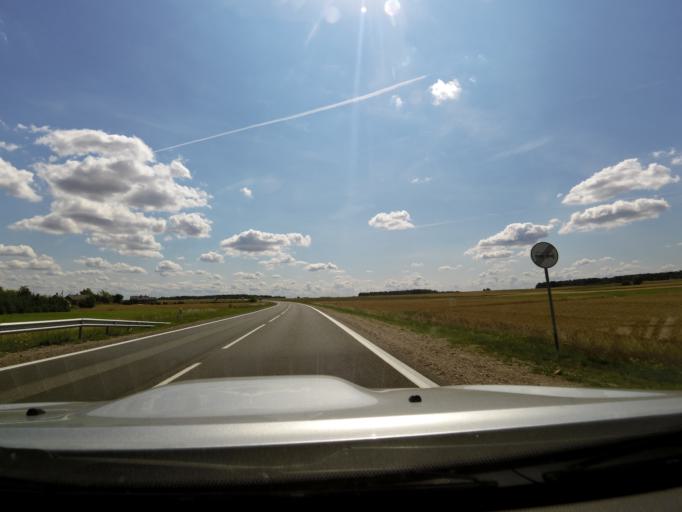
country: LT
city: Birstonas
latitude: 54.5859
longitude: 24.0391
